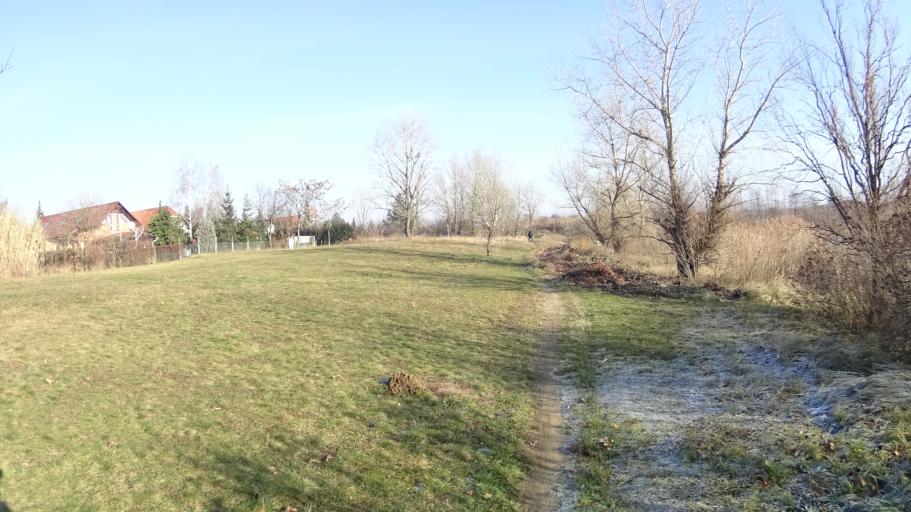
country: HU
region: Borsod-Abauj-Zemplen
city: Nyekladhaza
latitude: 47.9920
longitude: 20.8656
